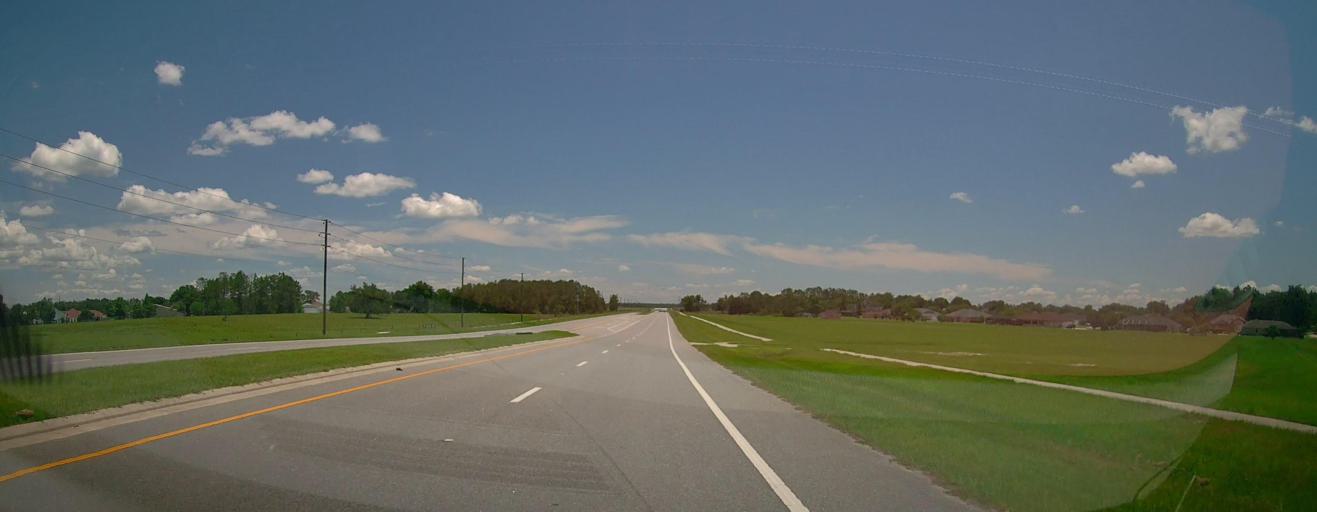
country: US
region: Florida
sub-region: Marion County
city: Silver Springs Shores
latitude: 29.0832
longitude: -82.0409
